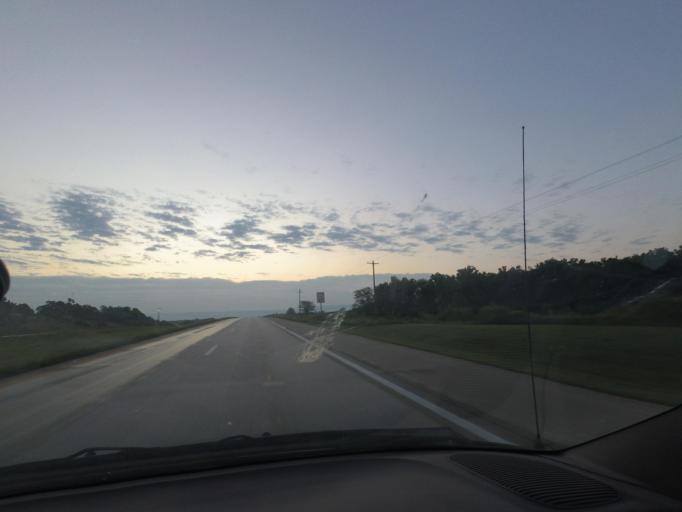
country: US
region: Missouri
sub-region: Macon County
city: Macon
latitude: 39.7591
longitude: -92.6667
